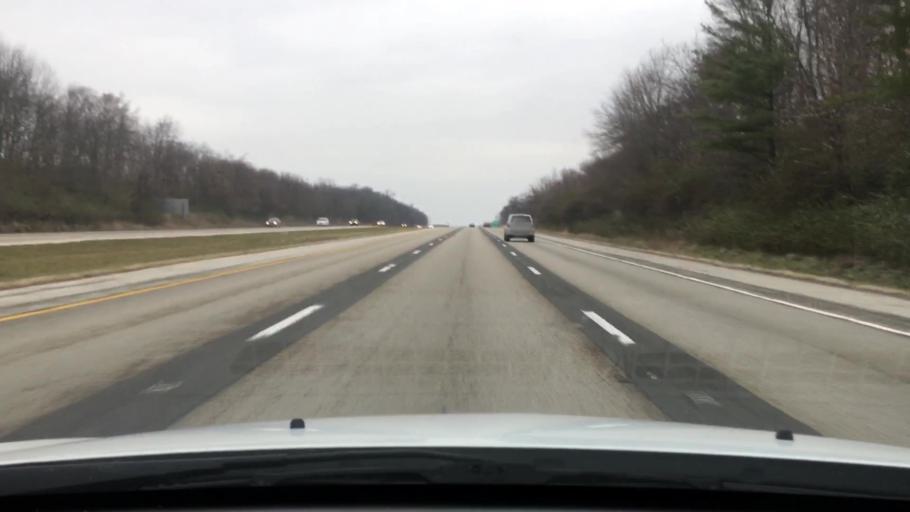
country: US
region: Illinois
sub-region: Logan County
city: Lincoln
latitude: 40.1474
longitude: -89.4172
